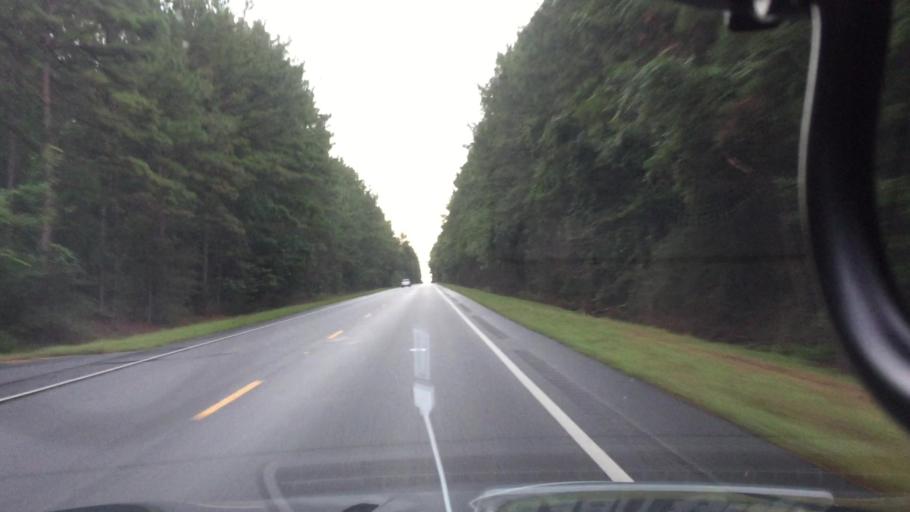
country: US
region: Alabama
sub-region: Coffee County
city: New Brockton
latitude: 31.4576
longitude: -85.8977
